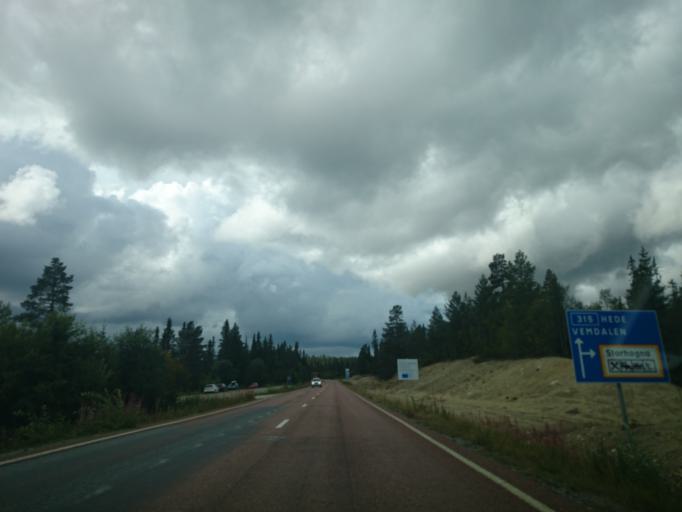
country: SE
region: Jaemtland
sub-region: Bergs Kommun
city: Hoverberg
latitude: 62.4775
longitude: 14.1372
